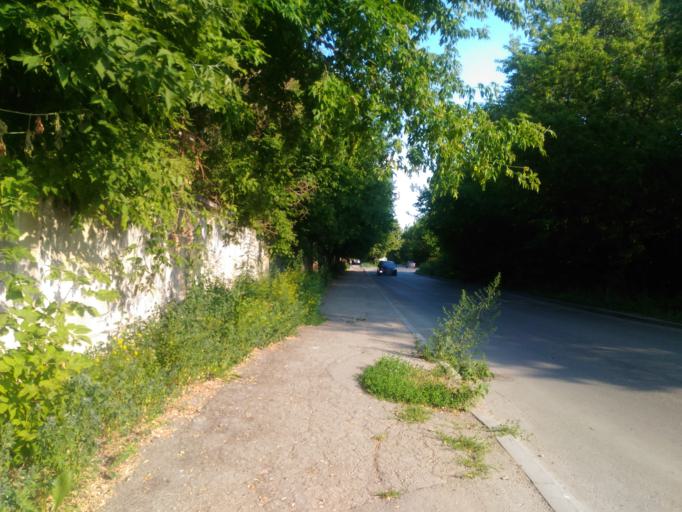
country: RU
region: Ulyanovsk
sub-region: Ulyanovskiy Rayon
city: Ulyanovsk
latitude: 54.3346
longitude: 48.3647
